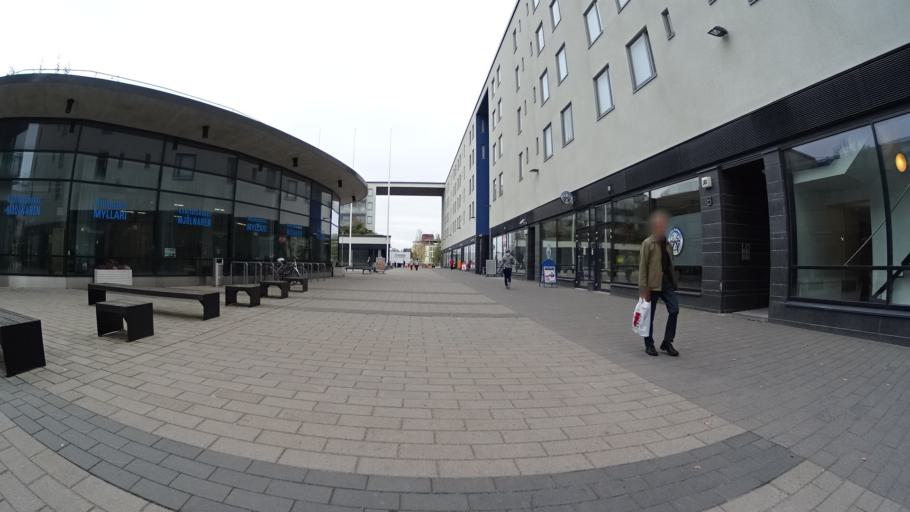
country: FI
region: Uusimaa
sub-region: Helsinki
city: Vantaa
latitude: 60.2239
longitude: 25.0728
